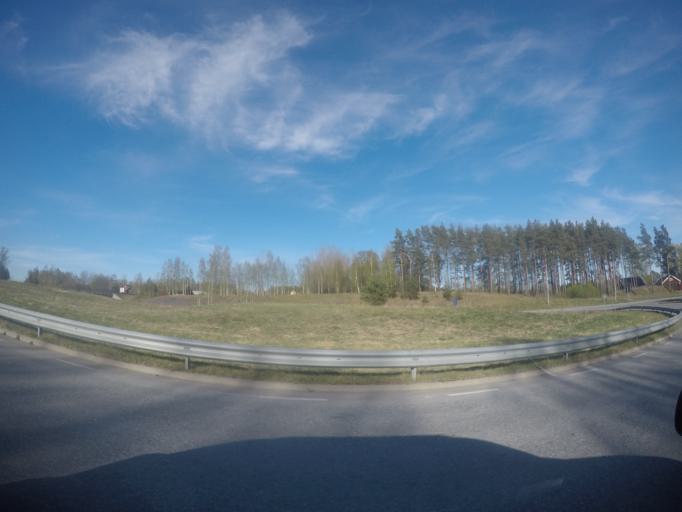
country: SE
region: OErebro
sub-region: Lindesbergs Kommun
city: Frovi
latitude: 59.3168
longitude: 15.4107
